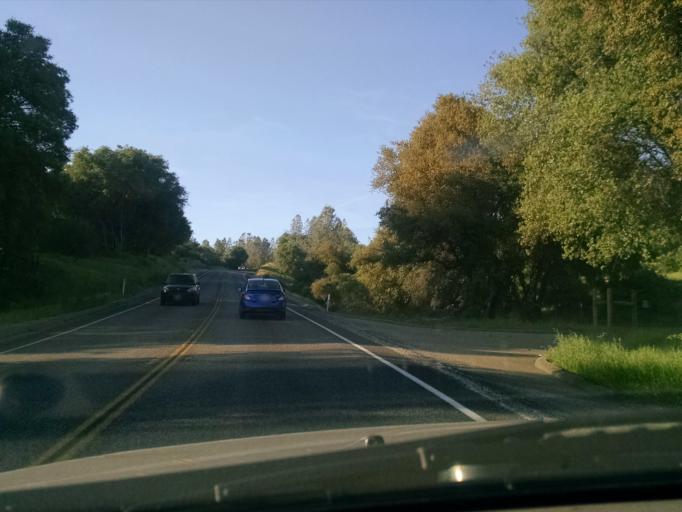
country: US
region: California
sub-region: Madera County
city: Ahwahnee
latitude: 37.3868
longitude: -119.7372
